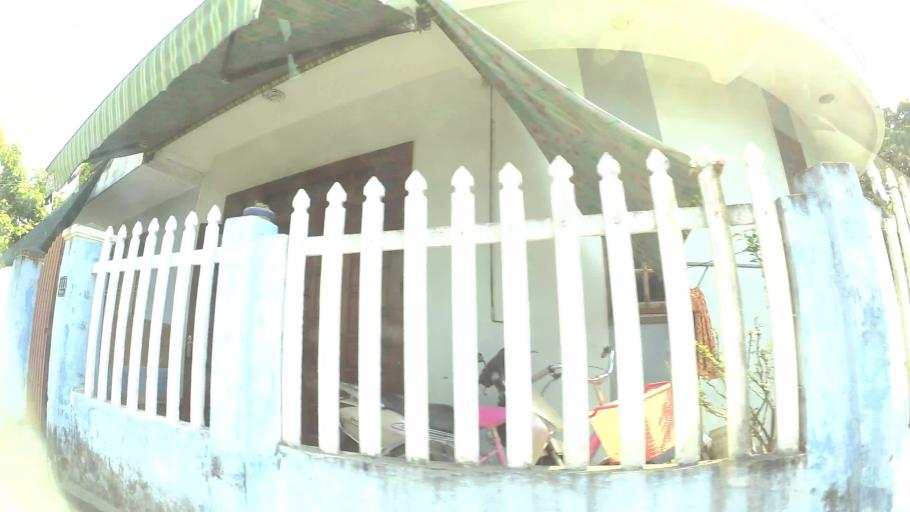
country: VN
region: Da Nang
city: Cam Le
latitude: 16.0130
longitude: 108.2001
